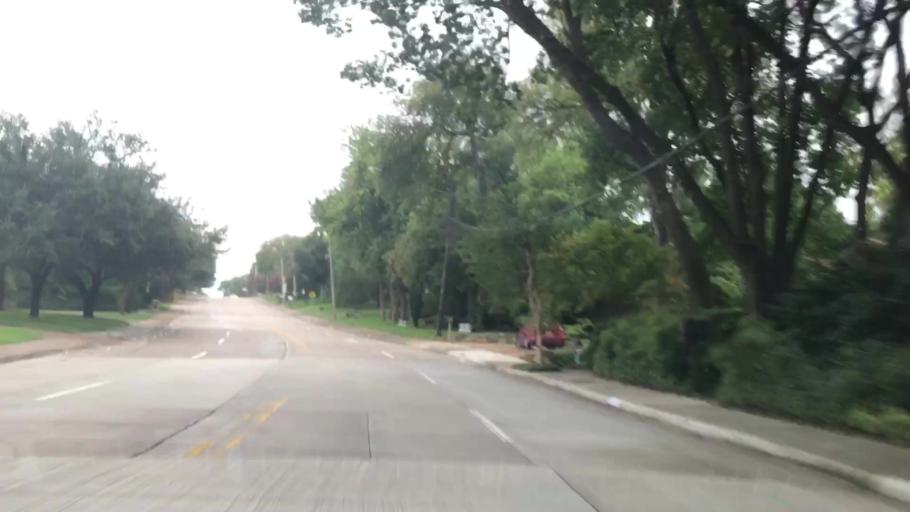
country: US
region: Texas
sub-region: Dallas County
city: Richardson
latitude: 32.9006
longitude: -96.7461
